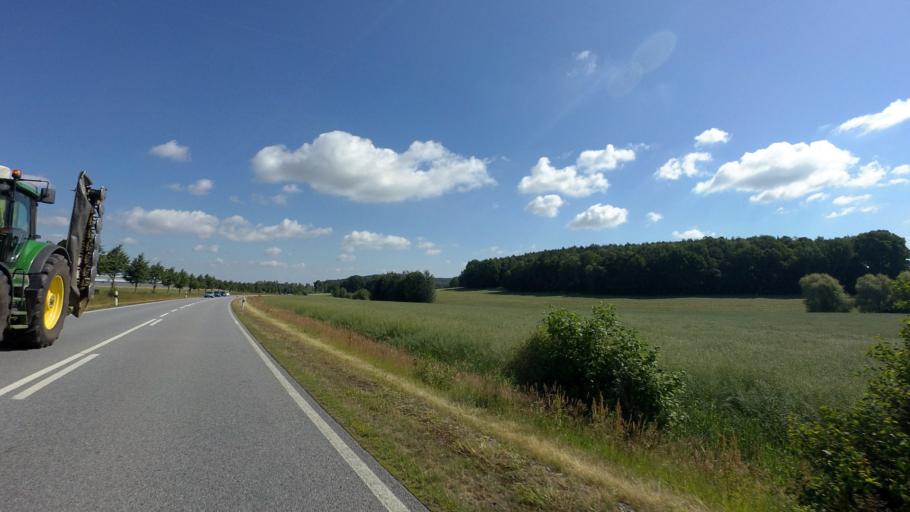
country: DE
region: Saxony
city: Elstra
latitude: 51.1860
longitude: 14.1386
